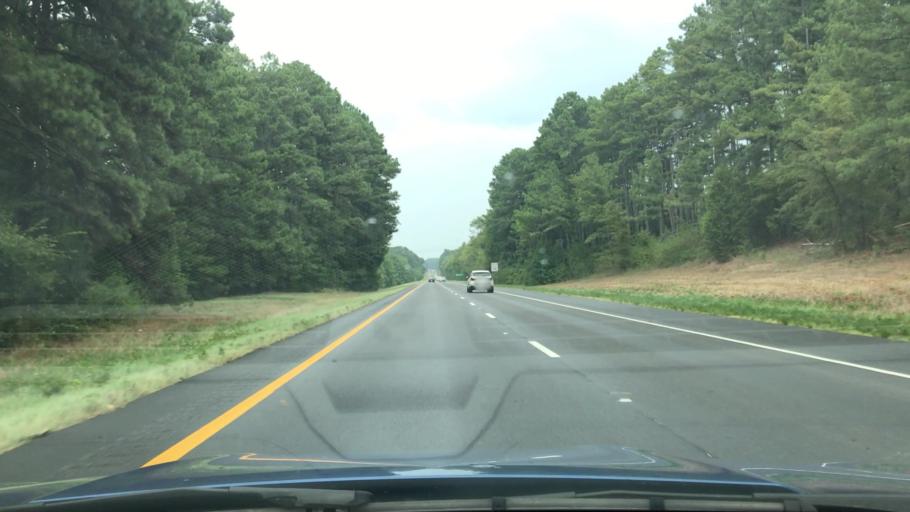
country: US
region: Texas
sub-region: Harrison County
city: Marshall
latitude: 32.4865
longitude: -94.4586
